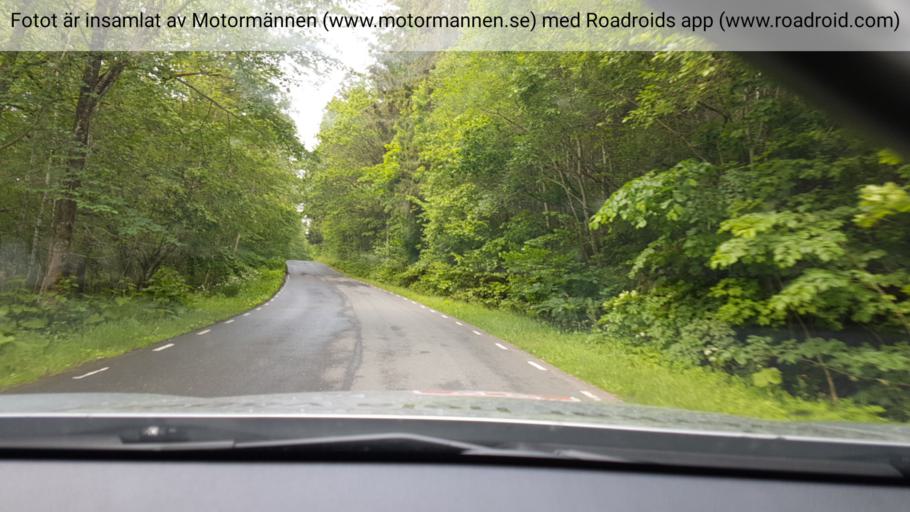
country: SE
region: Vaestra Goetaland
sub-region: Skovde Kommun
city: Skultorp
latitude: 58.3693
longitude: 13.8021
